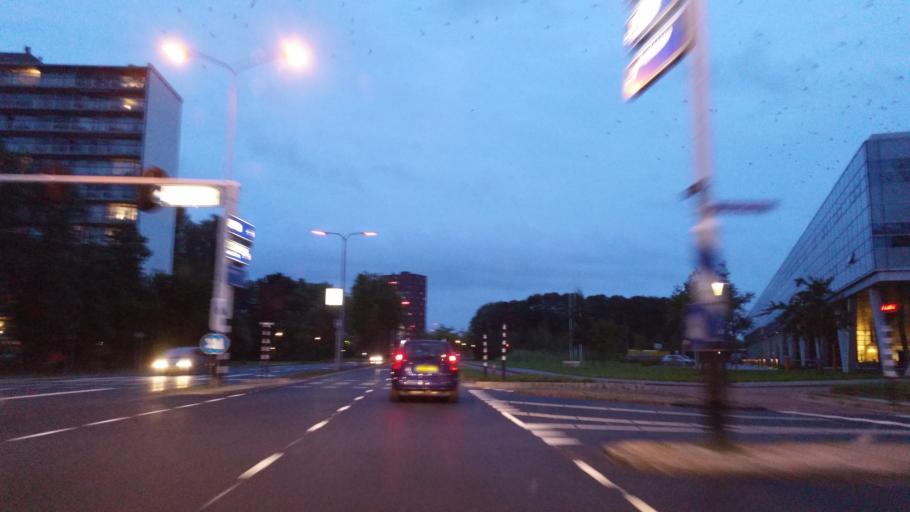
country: NL
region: Friesland
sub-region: Gemeente Leeuwarden
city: Bilgaard
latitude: 53.2132
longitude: 5.7976
